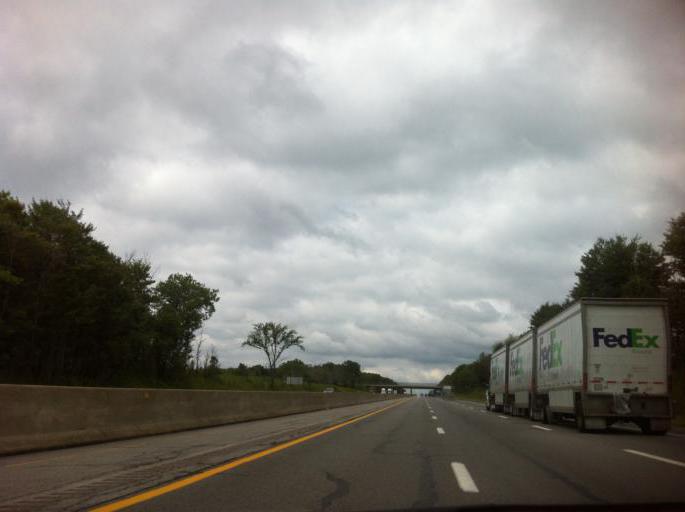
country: US
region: Ohio
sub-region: Portage County
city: Hiram
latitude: 41.2435
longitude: -81.1562
